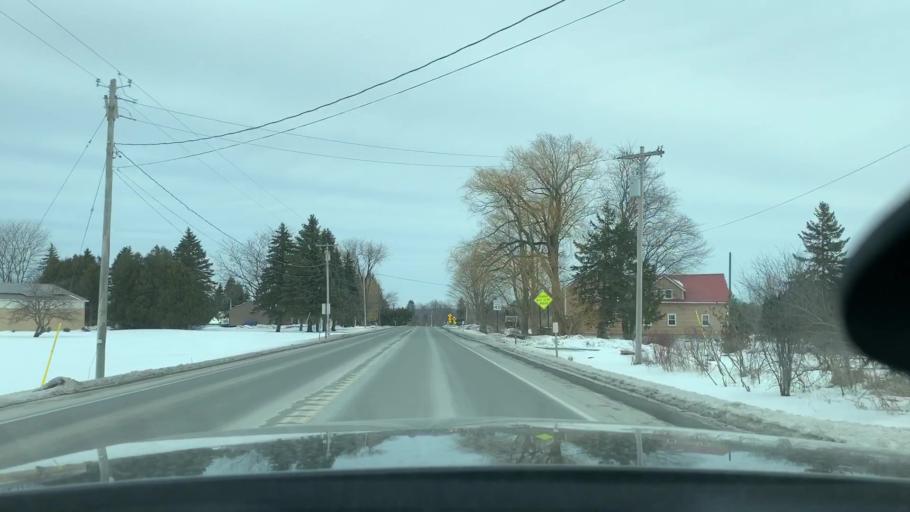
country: US
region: New York
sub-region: Herkimer County
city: Frankfort
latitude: 43.0333
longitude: -75.1091
